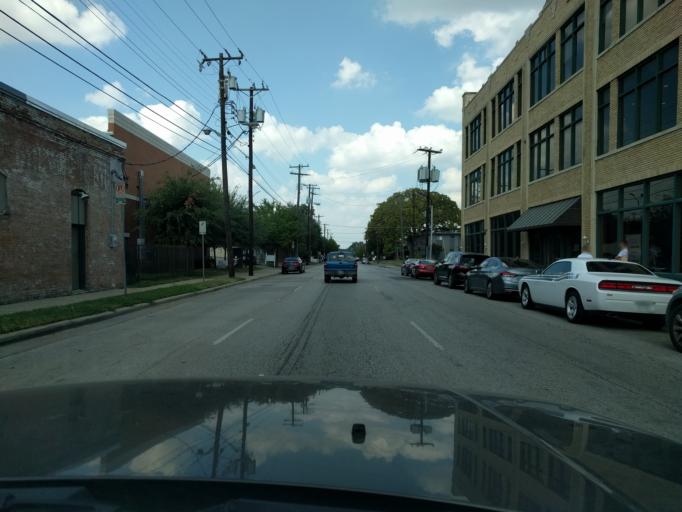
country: US
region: Texas
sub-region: Dallas County
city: Dallas
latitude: 32.7990
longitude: -96.7796
